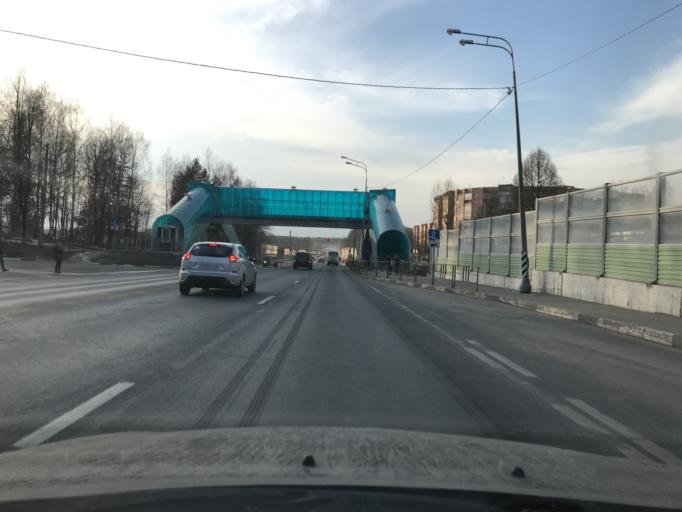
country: RU
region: Kaluga
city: Mstikhino
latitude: 54.5309
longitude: 36.1715
